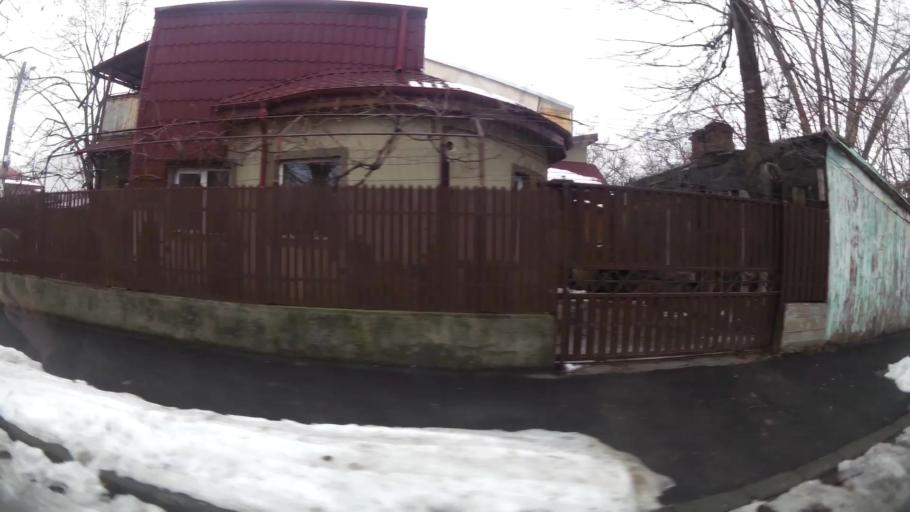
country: RO
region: Ilfov
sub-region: Comuna Chiajna
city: Rosu
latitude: 44.4695
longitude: 26.0326
